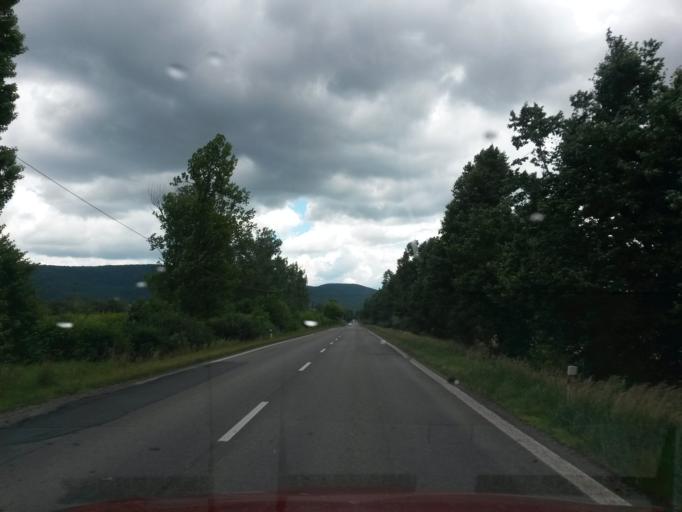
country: SK
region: Kosicky
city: Strazske
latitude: 48.8700
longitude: 21.8169
